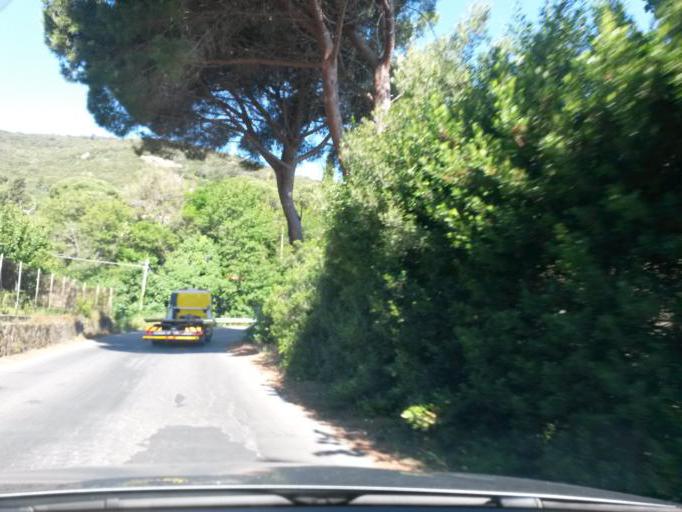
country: IT
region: Tuscany
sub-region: Provincia di Livorno
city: Marciana Marina
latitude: 42.7947
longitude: 10.2164
